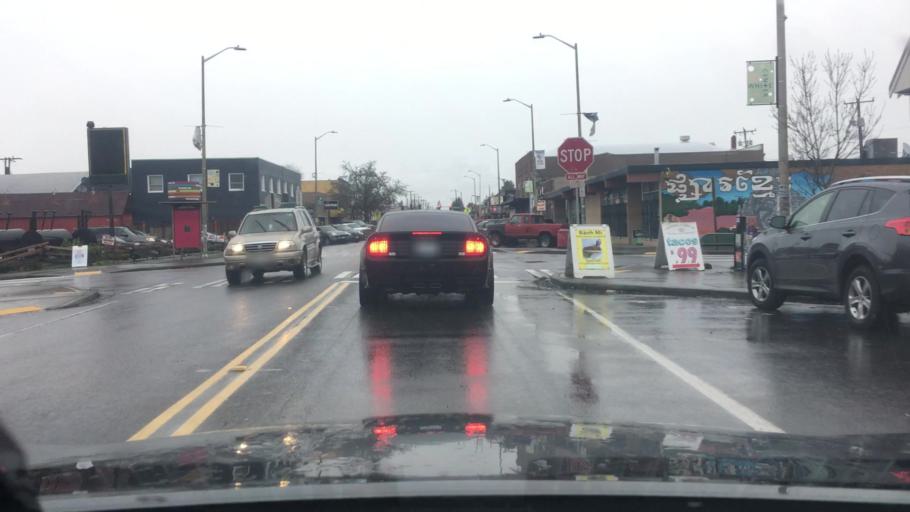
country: US
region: Washington
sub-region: King County
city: White Center
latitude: 47.5153
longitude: -122.3551
